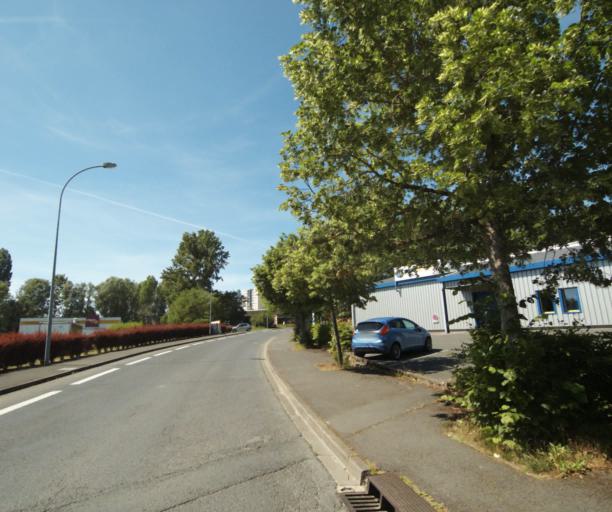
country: FR
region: Champagne-Ardenne
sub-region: Departement des Ardennes
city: Villers-Semeuse
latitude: 49.7464
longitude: 4.7281
